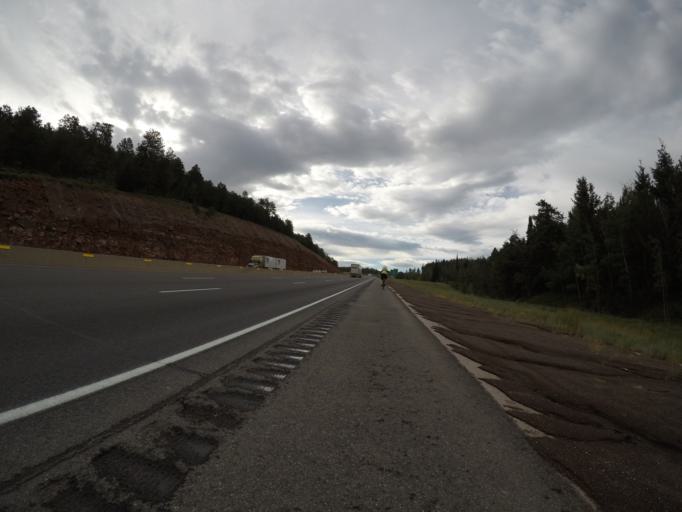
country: US
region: Wyoming
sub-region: Albany County
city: Laramie
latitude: 41.2575
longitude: -105.4522
